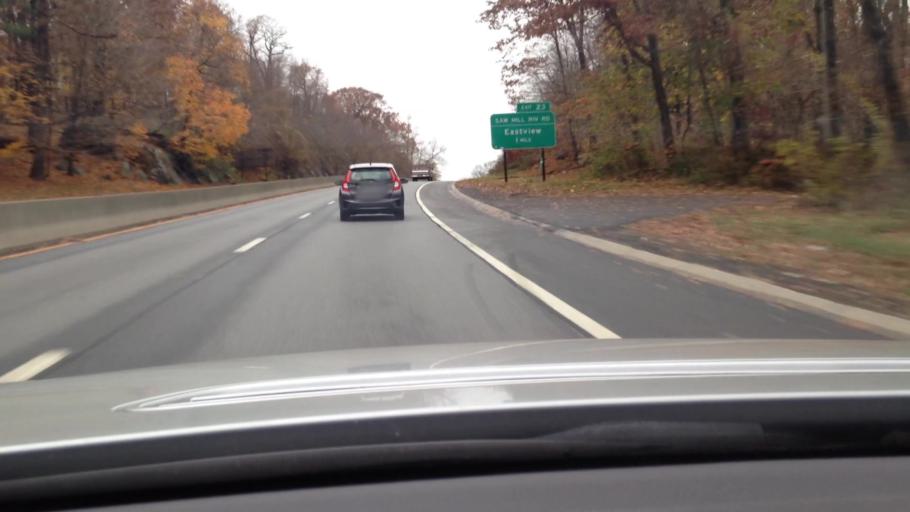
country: US
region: New York
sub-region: Westchester County
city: Elmsford
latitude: 41.0662
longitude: -73.8262
